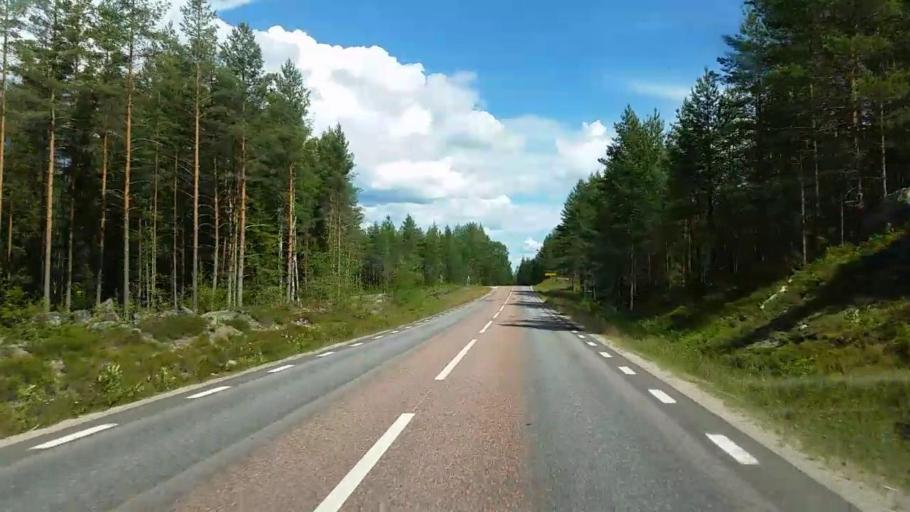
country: SE
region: Gaevleborg
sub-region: Ovanakers Kommun
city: Edsbyn
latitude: 61.3318
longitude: 15.5317
